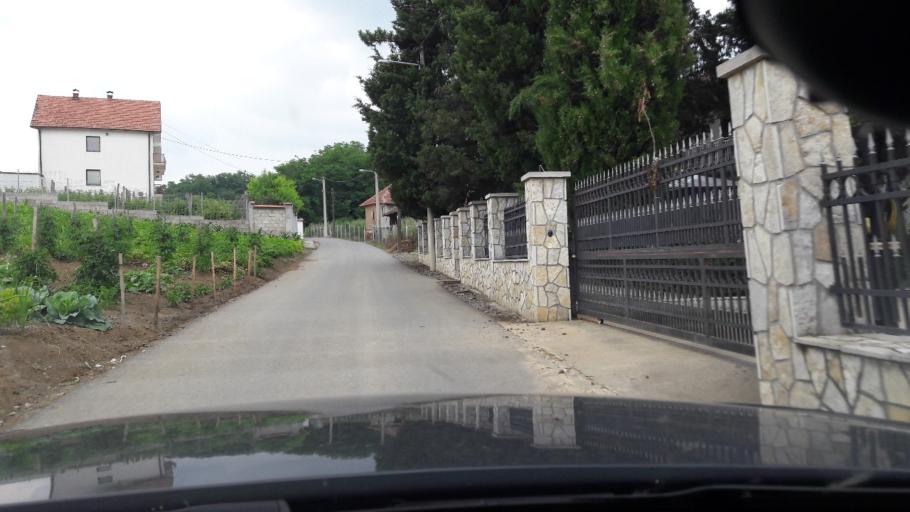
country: RS
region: Central Serbia
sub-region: Belgrade
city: Sopot
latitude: 44.6408
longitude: 20.5932
